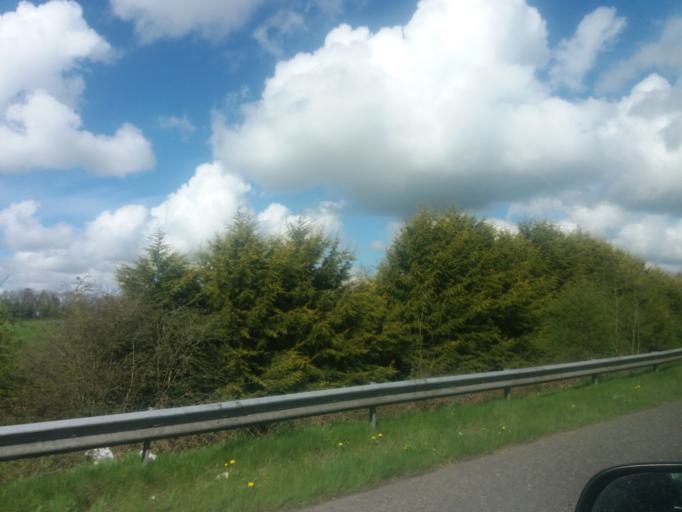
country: IE
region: Ulster
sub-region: An Cabhan
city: Virginia
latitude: 53.8619
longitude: -7.1111
